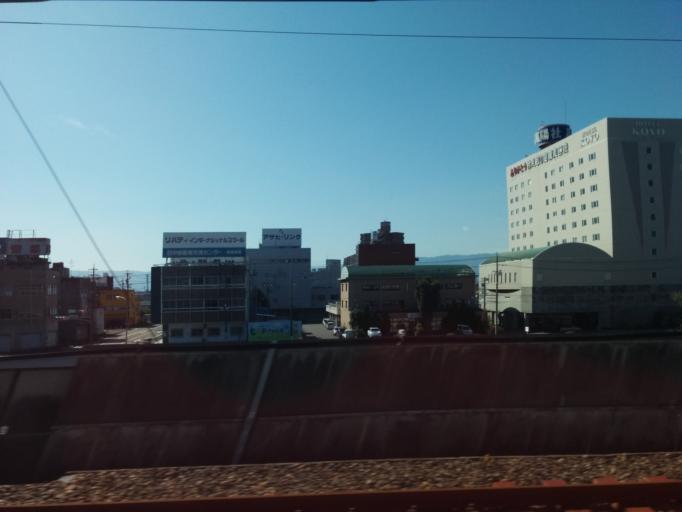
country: JP
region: Gifu
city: Ogaki
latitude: 35.3173
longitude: 136.6838
